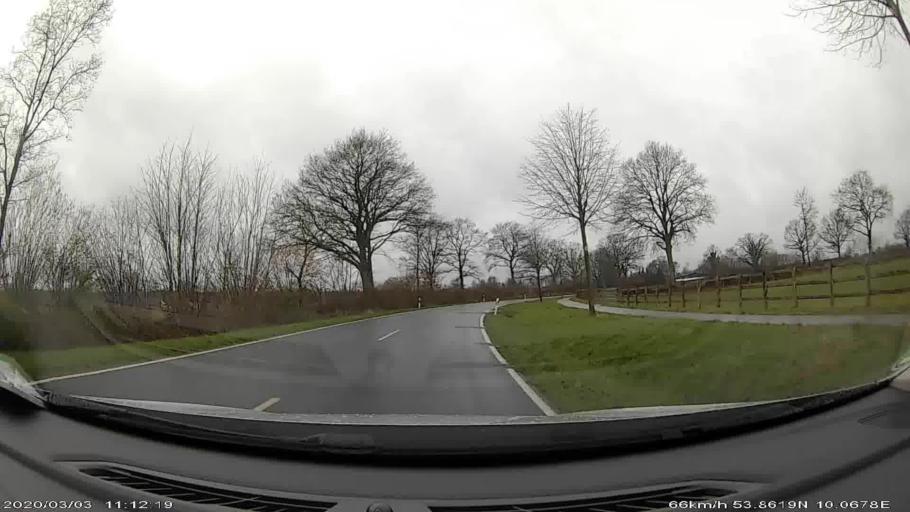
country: DE
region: Schleswig-Holstein
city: Struvenhutten
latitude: 53.8629
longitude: 10.0633
